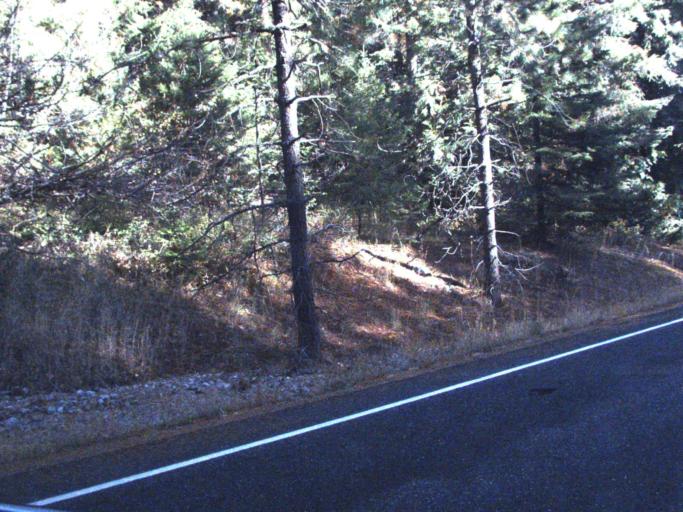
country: US
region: Washington
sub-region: Stevens County
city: Kettle Falls
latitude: 48.5935
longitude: -118.3283
